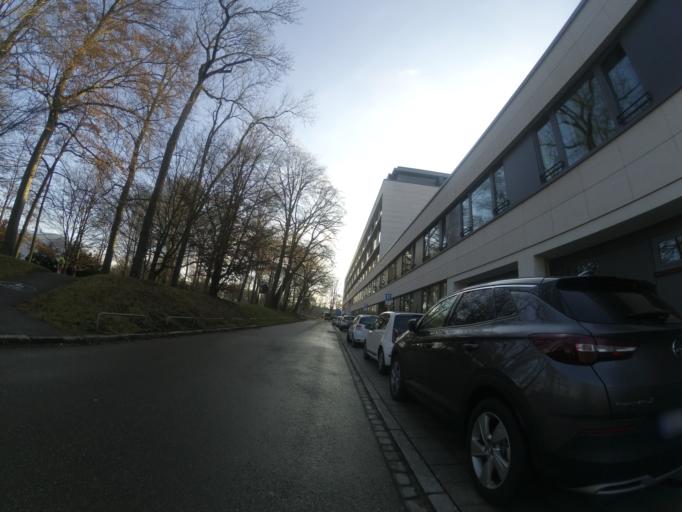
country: DE
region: Bavaria
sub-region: Swabia
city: Neu-Ulm
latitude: 48.4021
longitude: 10.0073
